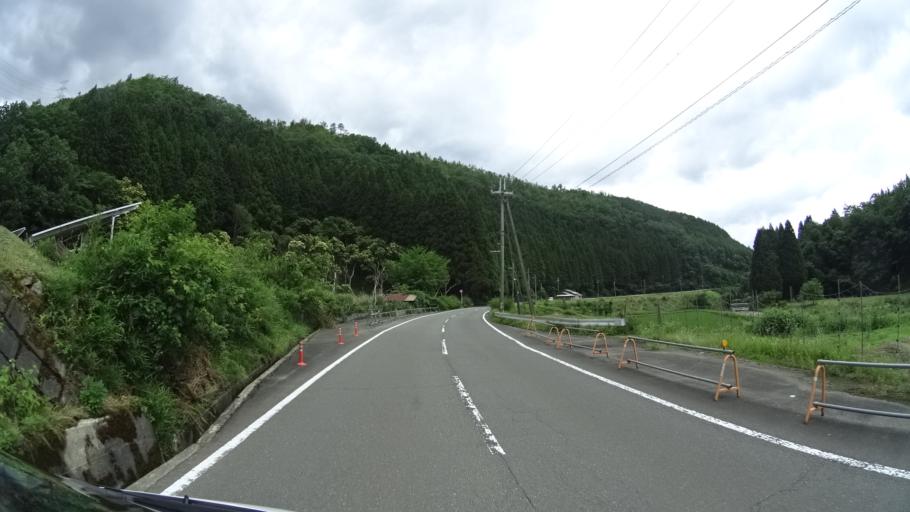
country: JP
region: Kyoto
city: Kameoka
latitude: 35.0754
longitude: 135.4101
